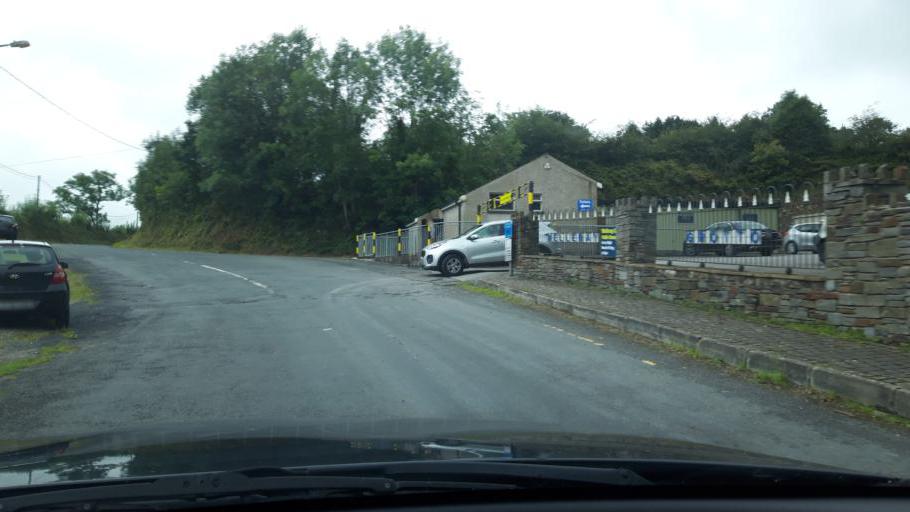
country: IE
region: Munster
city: Cahir
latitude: 52.1724
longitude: -7.8541
